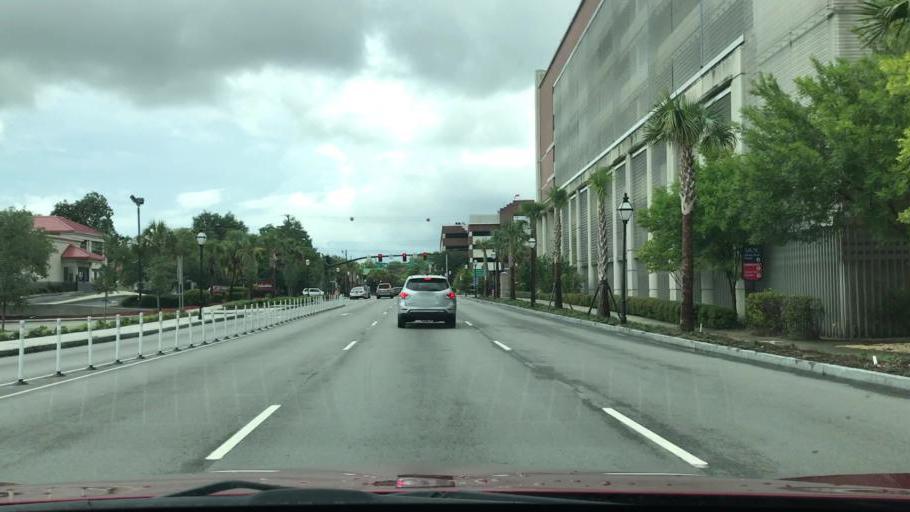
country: US
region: South Carolina
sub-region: Charleston County
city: Charleston
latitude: 32.7864
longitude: -79.9536
